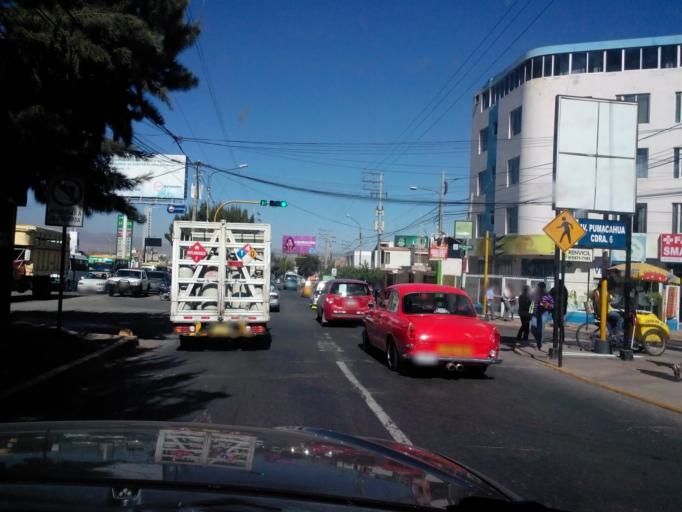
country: PE
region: Arequipa
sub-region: Provincia de Arequipa
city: Arequipa
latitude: -16.3755
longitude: -71.5578
